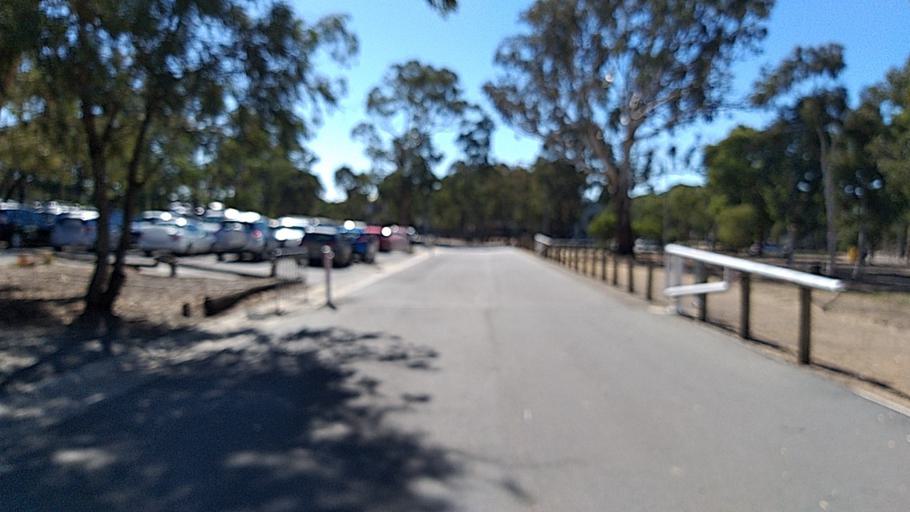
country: AU
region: Australian Capital Territory
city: Kaleen
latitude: -35.2467
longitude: 149.1001
